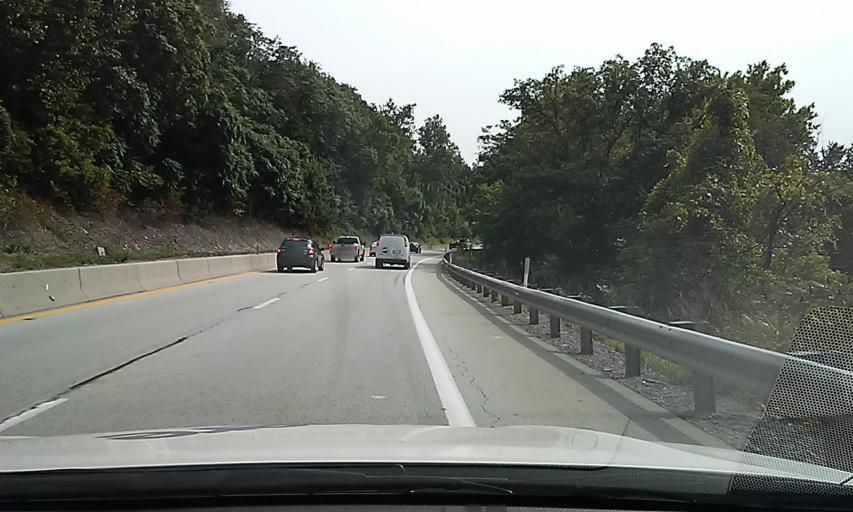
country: US
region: Pennsylvania
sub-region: Fayette County
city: Connellsville
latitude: 40.0294
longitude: -79.5881
